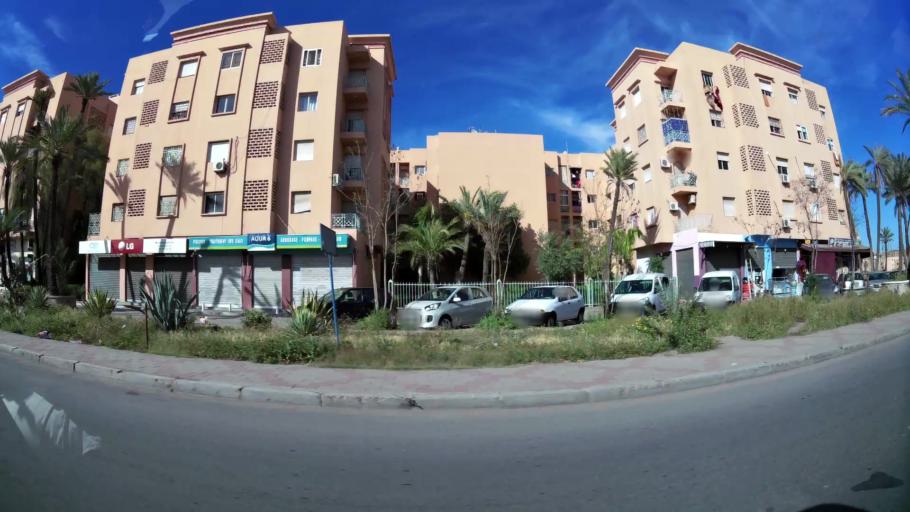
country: MA
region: Marrakech-Tensift-Al Haouz
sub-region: Marrakech
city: Marrakesh
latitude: 31.6621
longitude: -8.0282
